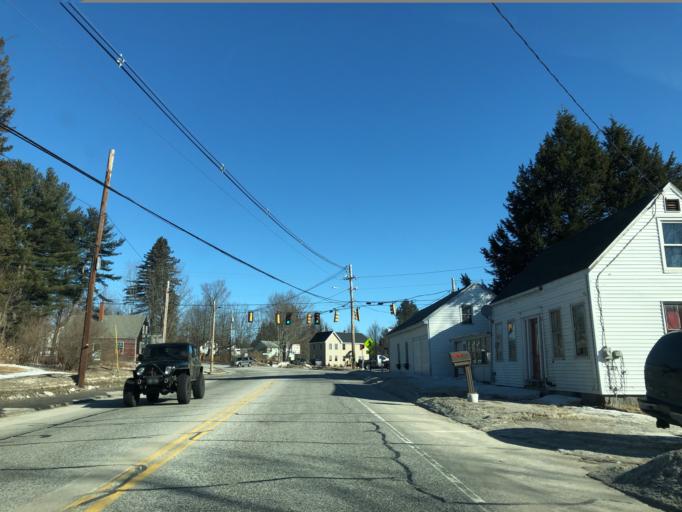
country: US
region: Maine
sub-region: Cumberland County
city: North Windham
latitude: 43.7889
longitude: -70.4090
